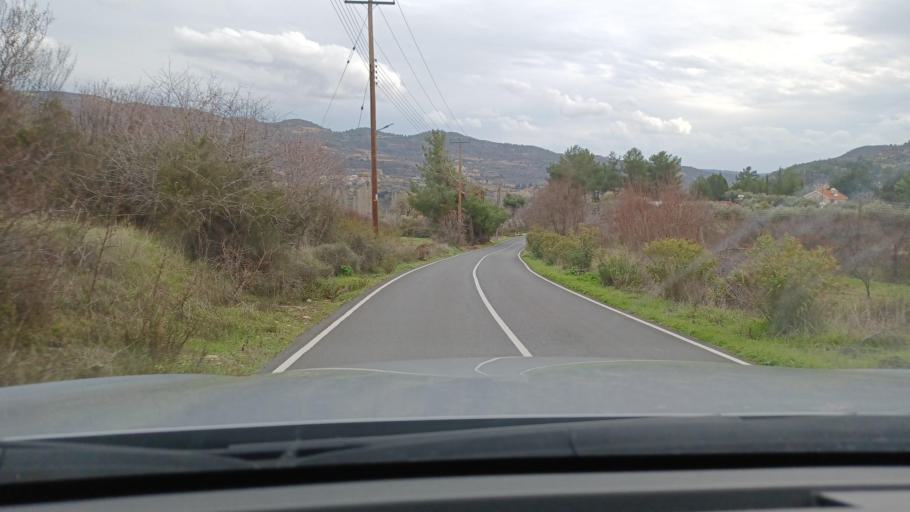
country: CY
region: Limassol
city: Pelendri
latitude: 34.8229
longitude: 32.8968
